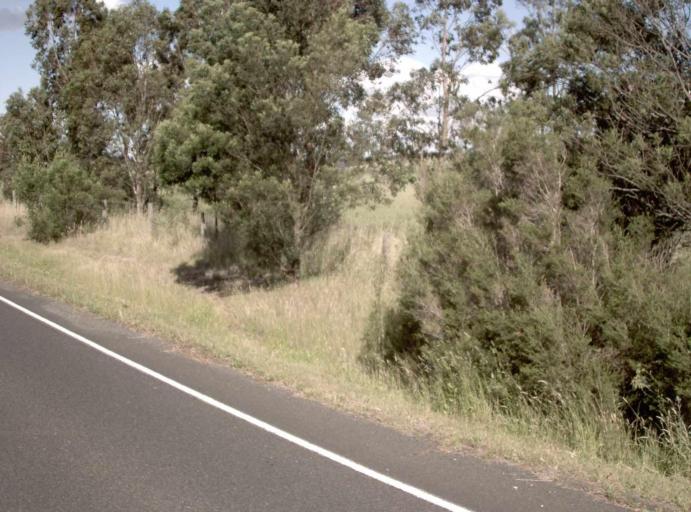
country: AU
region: Victoria
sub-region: Latrobe
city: Morwell
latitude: -38.1708
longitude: 146.4081
